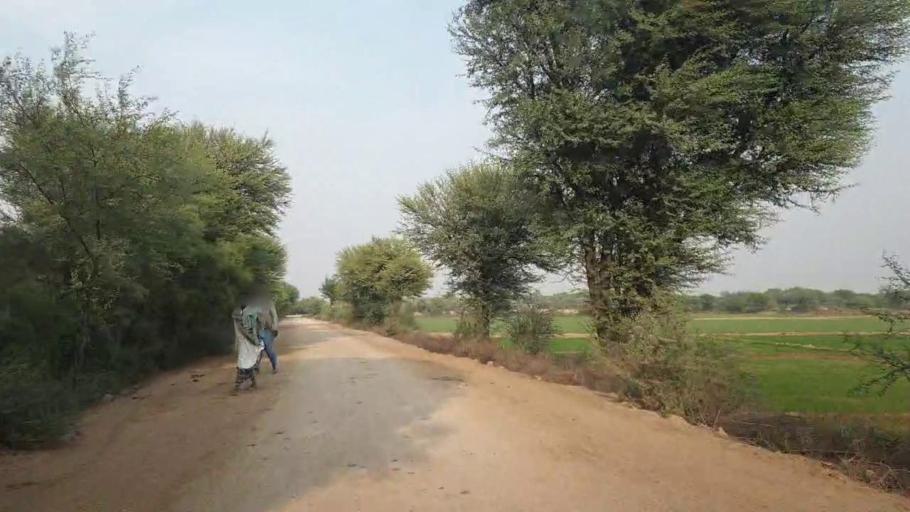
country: PK
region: Sindh
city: Sann
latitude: 26.1252
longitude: 68.0632
